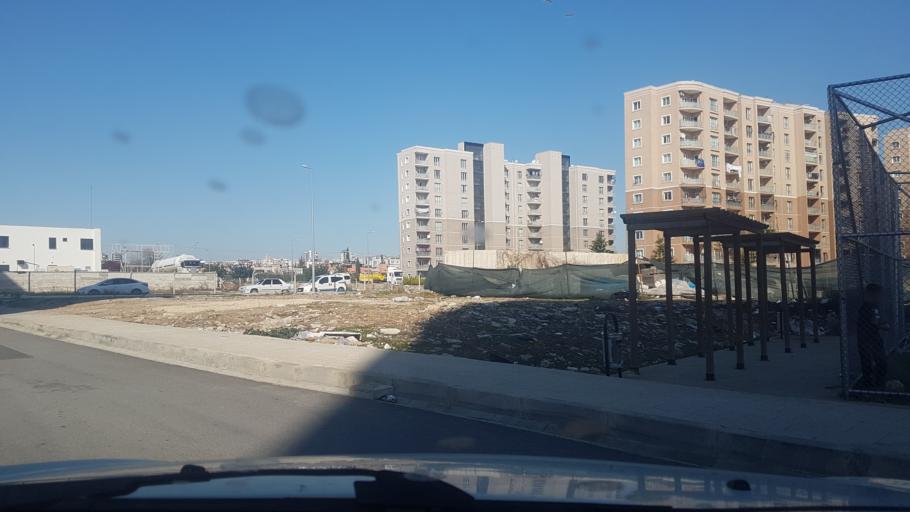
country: TR
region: Adana
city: Seyhan
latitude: 37.0094
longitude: 35.2758
